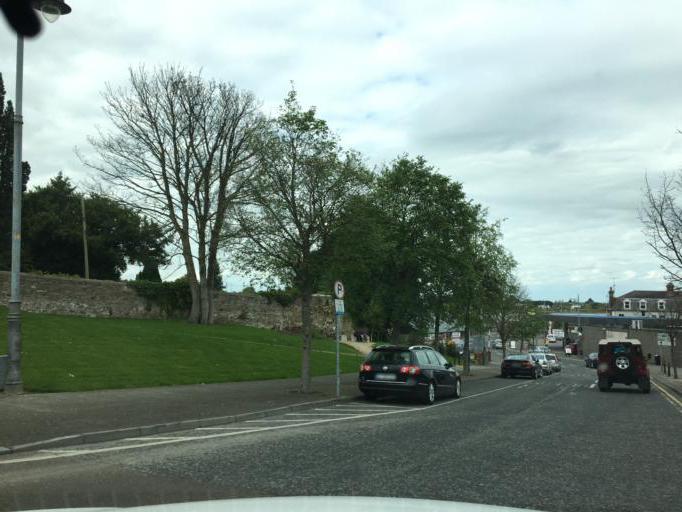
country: IE
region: Leinster
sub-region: Loch Garman
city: Loch Garman
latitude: 52.3424
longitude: -6.4679
